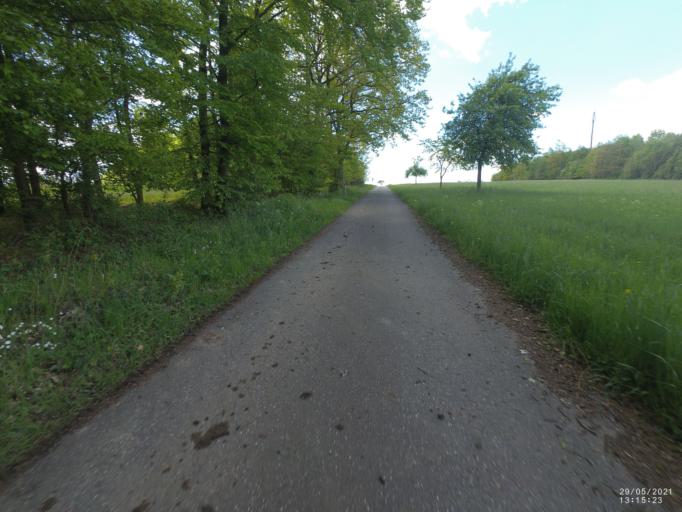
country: DE
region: Rheinland-Pfalz
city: Nortershausen
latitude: 50.2345
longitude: 7.4961
